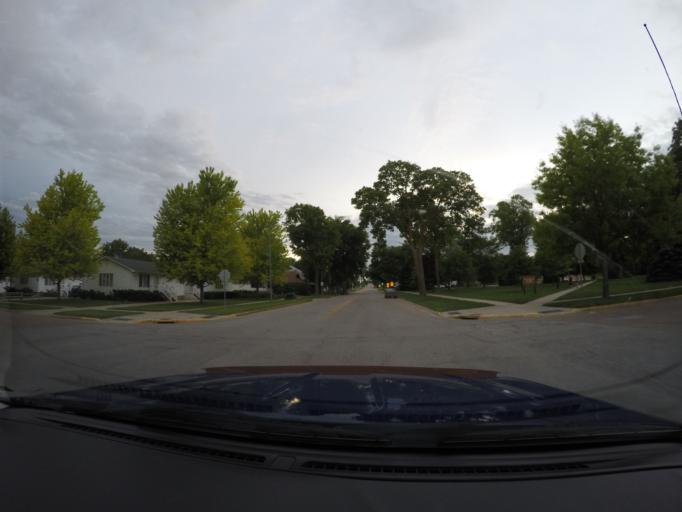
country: US
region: Nebraska
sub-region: Buffalo County
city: Kearney
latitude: 40.7046
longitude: -99.0883
